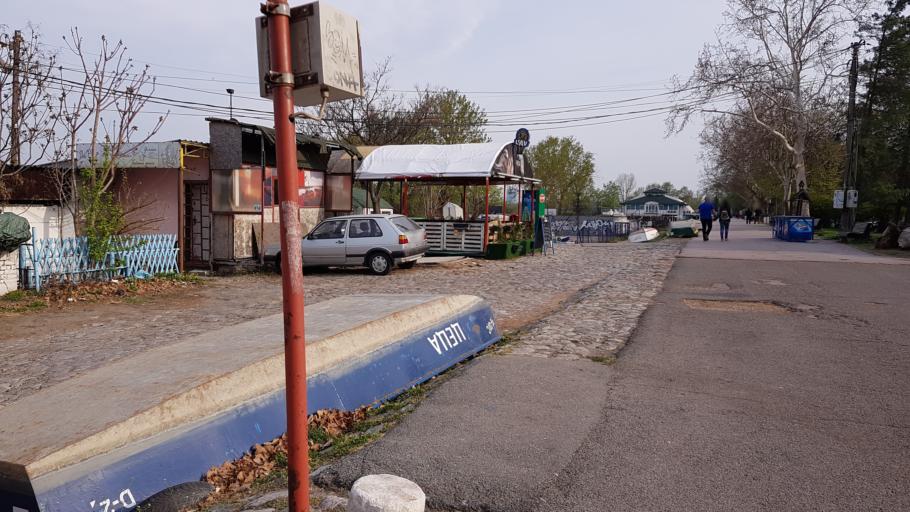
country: RS
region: Central Serbia
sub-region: Belgrade
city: Zemun
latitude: 44.8425
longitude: 20.4176
